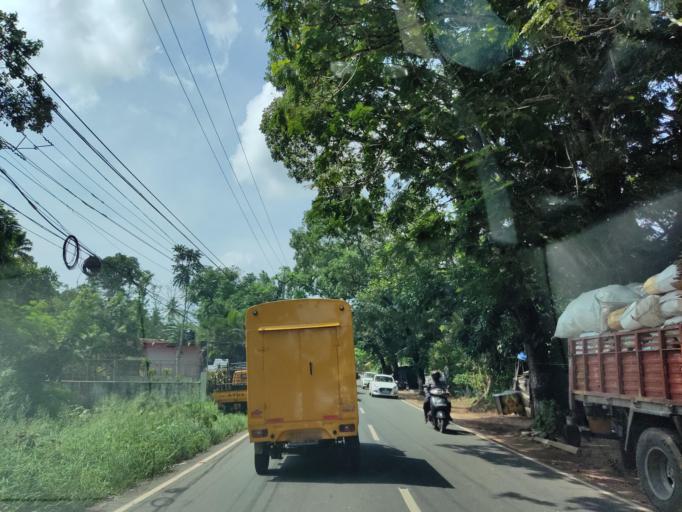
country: IN
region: Kerala
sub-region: Alappuzha
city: Mavelikara
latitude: 9.2732
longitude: 76.5361
